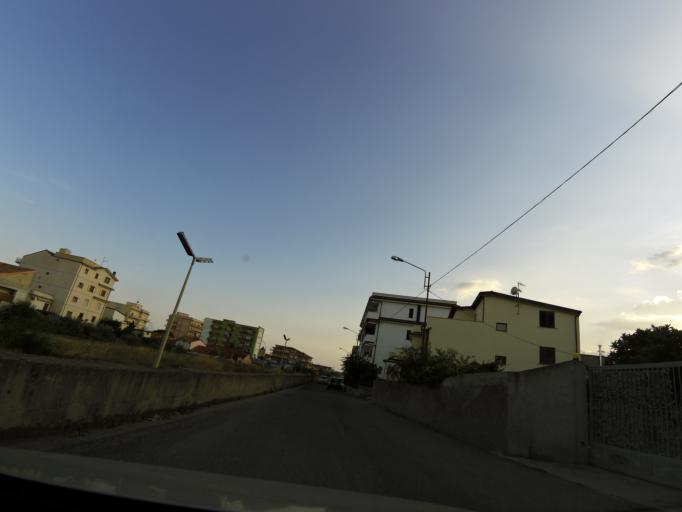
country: IT
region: Calabria
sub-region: Provincia di Reggio Calabria
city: Monasterace Marina
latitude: 38.4355
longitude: 16.5733
